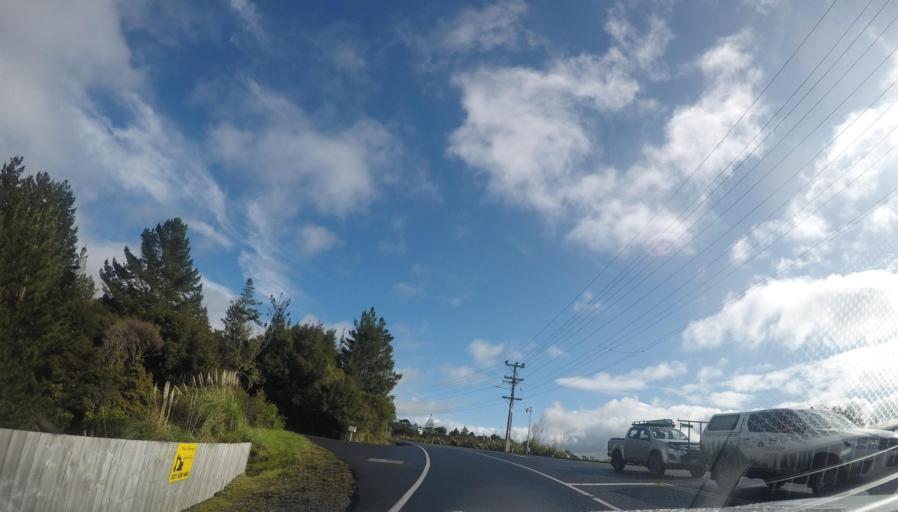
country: NZ
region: Auckland
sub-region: Auckland
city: Warkworth
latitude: -36.4076
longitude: 174.7192
